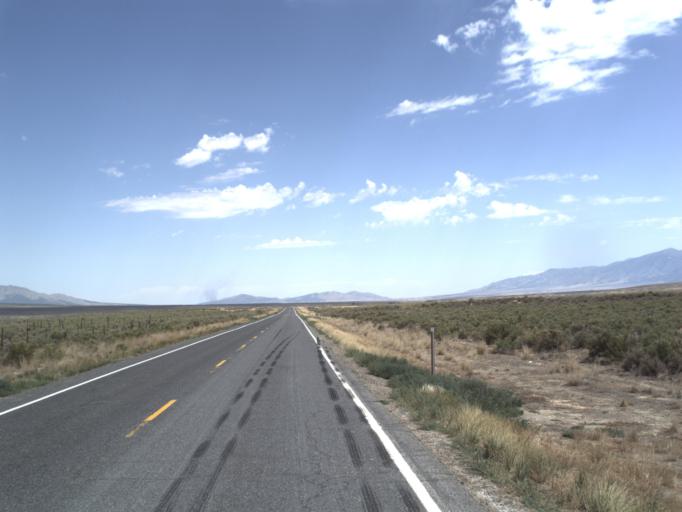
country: US
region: Utah
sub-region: Tooele County
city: Tooele
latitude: 40.1182
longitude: -112.4308
